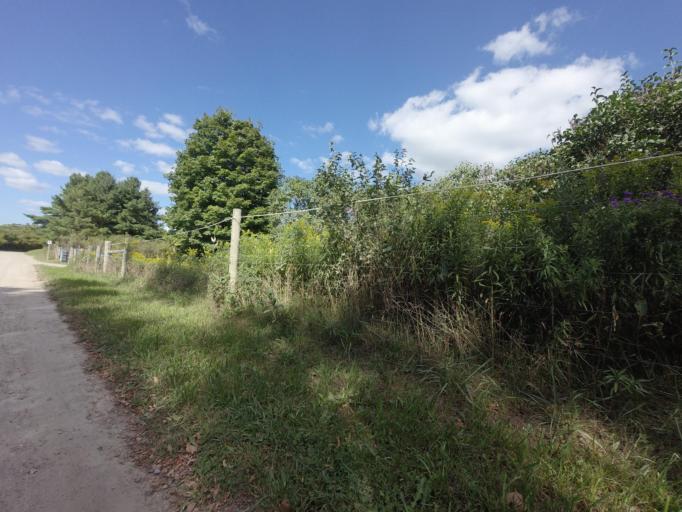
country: CA
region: Ontario
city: Orangeville
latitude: 43.8256
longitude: -80.0041
